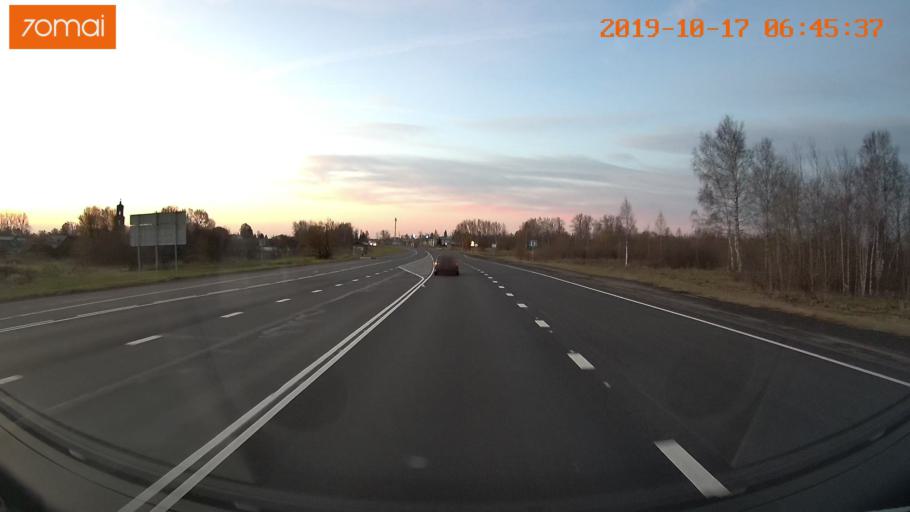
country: RU
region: Vladimir
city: Kideksha
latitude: 56.5579
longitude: 40.5479
